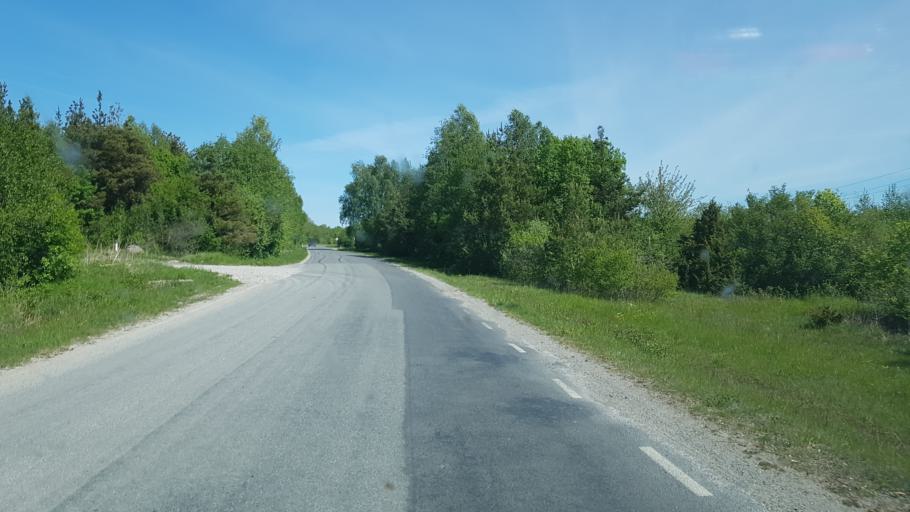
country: EE
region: Saare
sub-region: Kuressaare linn
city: Kuressaare
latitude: 58.2763
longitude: 22.5005
